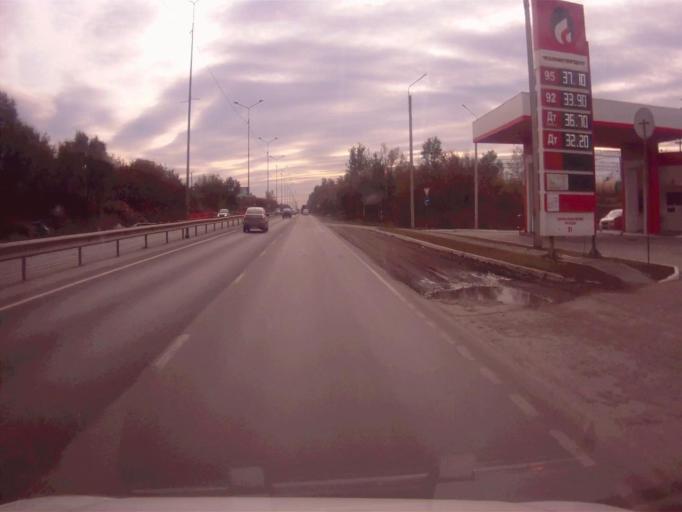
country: RU
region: Chelyabinsk
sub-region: Gorod Chelyabinsk
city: Chelyabinsk
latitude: 55.1068
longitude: 61.4076
